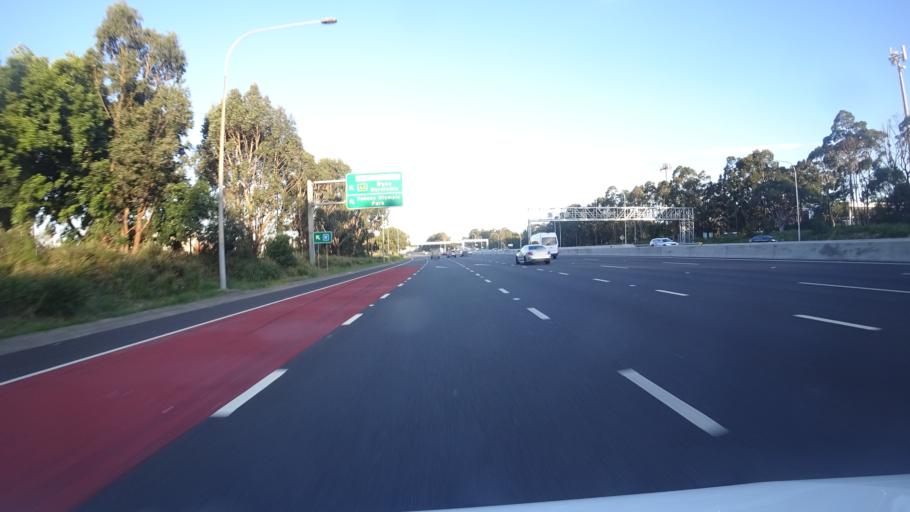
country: AU
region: New South Wales
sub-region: Strathfield
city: Homebush
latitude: -33.8556
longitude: 151.0651
